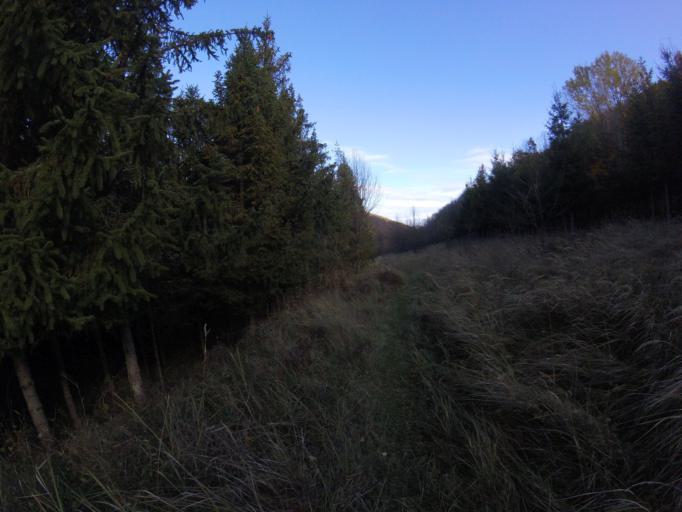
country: HU
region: Borsod-Abauj-Zemplen
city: Tolcsva
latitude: 48.3791
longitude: 21.3850
